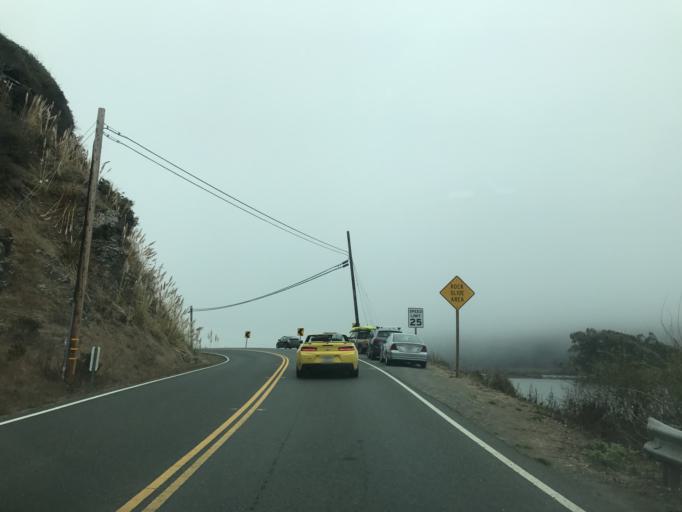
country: US
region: California
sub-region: Sonoma County
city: Monte Rio
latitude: 38.4490
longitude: -123.1147
